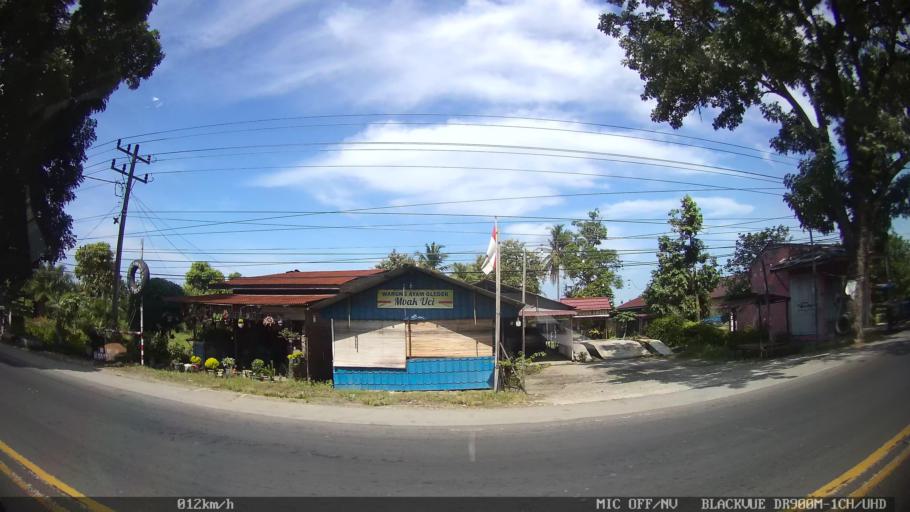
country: ID
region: North Sumatra
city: Binjai
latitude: 3.6698
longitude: 98.5088
